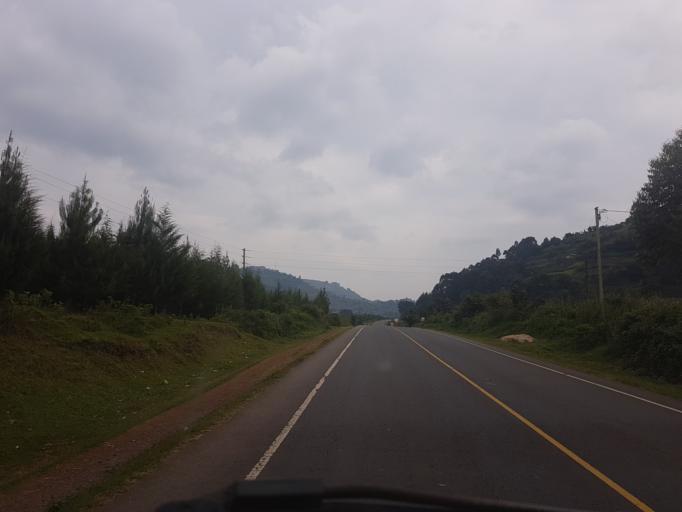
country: UG
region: Western Region
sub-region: Kisoro District
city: Kisoro
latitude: -1.2114
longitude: 29.8279
